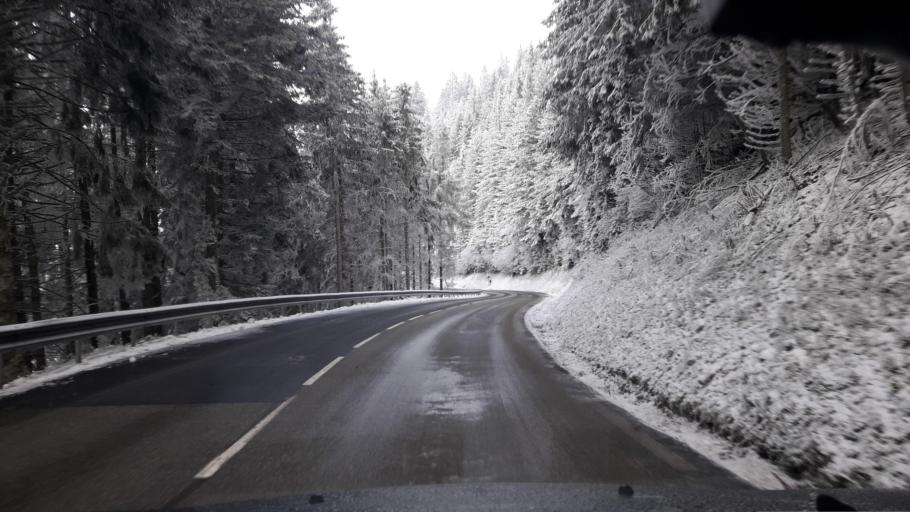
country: FR
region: Rhone-Alpes
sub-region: Departement de l'Isere
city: Allevard
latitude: 45.3946
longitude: 6.1034
